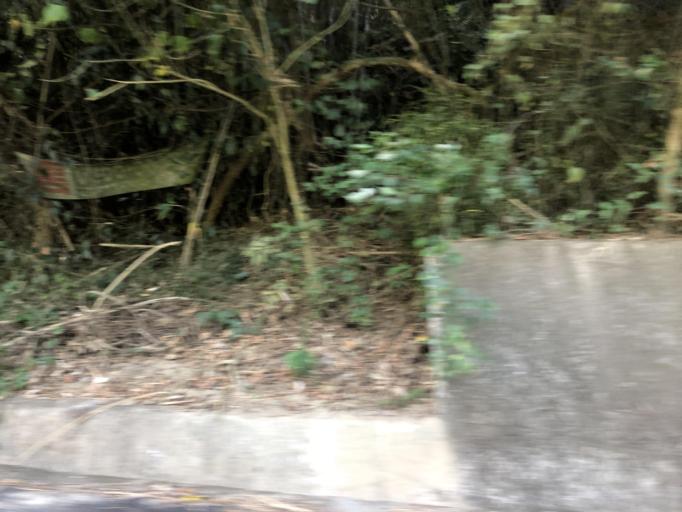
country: TW
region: Taiwan
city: Yujing
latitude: 23.0095
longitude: 120.3870
